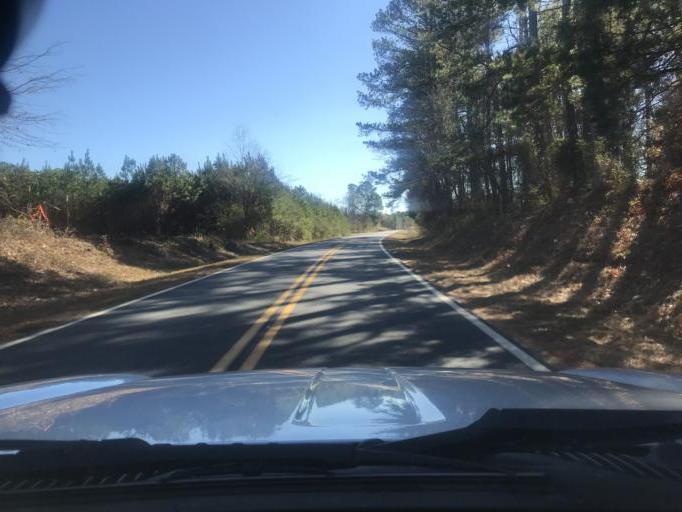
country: US
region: Georgia
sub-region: Barrow County
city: Winder
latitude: 33.9216
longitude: -83.7673
